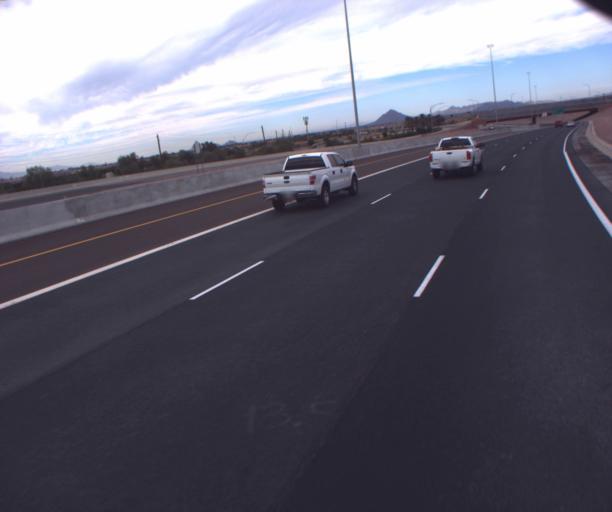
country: US
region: Arizona
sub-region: Maricopa County
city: Mesa
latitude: 33.4810
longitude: -111.7490
